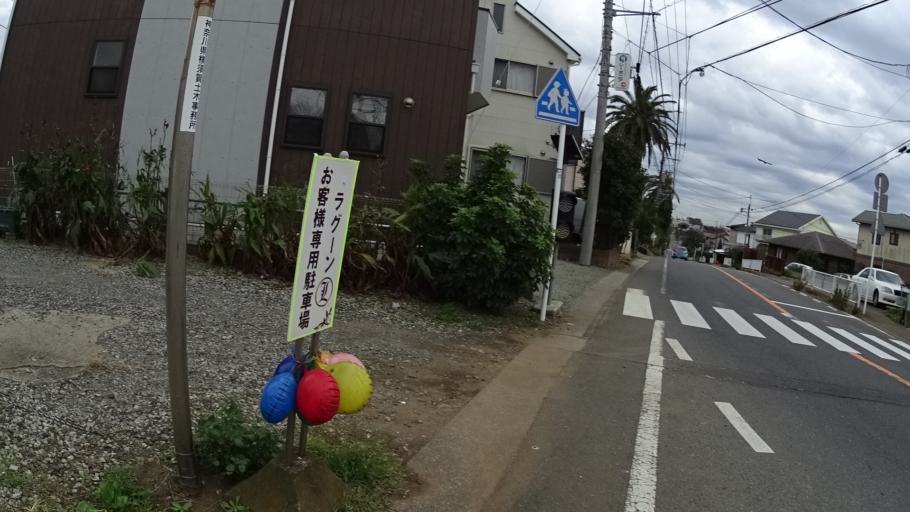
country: JP
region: Kanagawa
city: Miura
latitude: 35.1593
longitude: 139.6277
